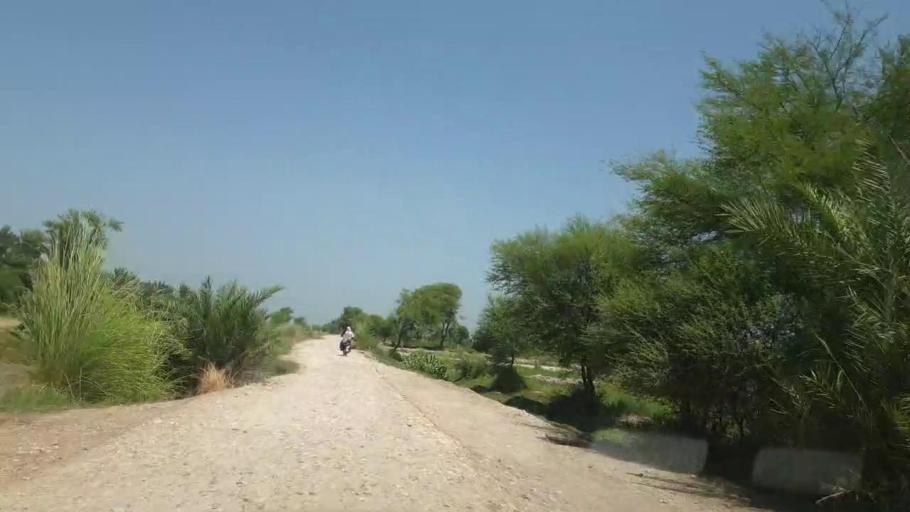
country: PK
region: Sindh
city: Pano Aqil
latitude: 27.6604
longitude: 69.1074
